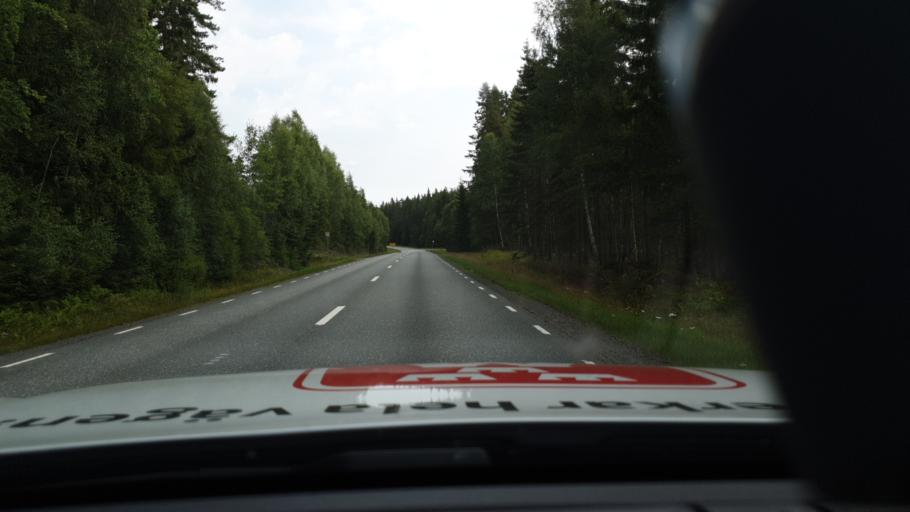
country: SE
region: Joenkoeping
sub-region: Aneby Kommun
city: Aneby
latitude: 57.8073
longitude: 14.7216
